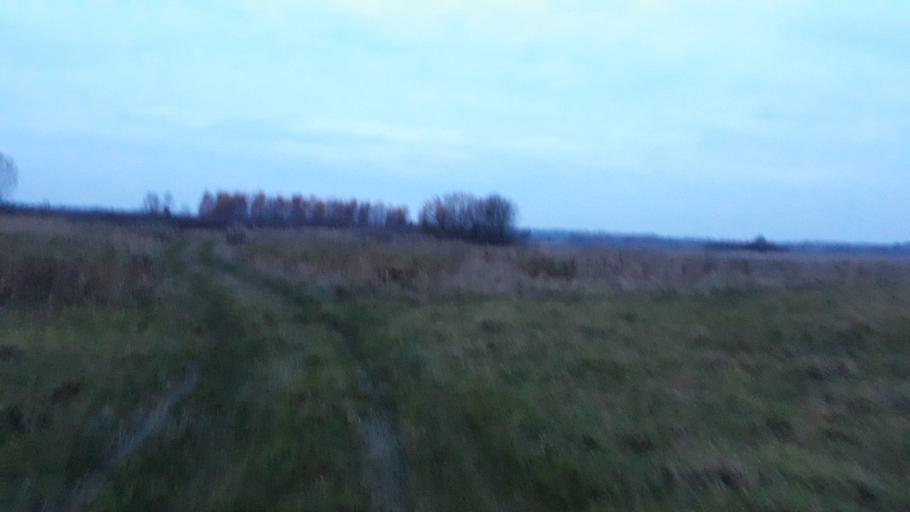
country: PL
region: Lublin Voivodeship
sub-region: Powiat janowski
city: Dzwola
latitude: 50.6616
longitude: 22.5985
